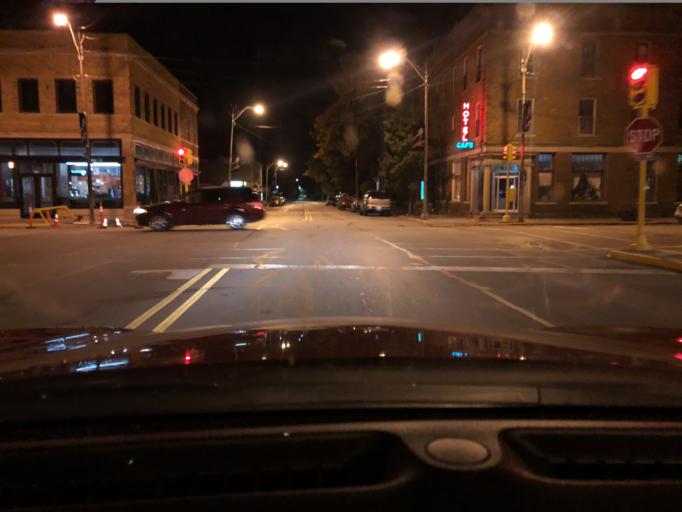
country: US
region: Indiana
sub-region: DeKalb County
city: Auburn
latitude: 41.3661
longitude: -85.0558
